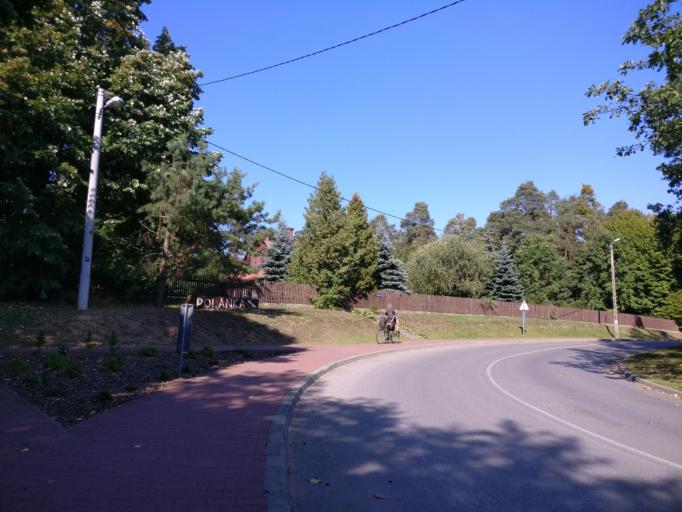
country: PL
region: Masovian Voivodeship
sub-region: Powiat kozienicki
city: Garbatka-Letnisko
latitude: 51.4930
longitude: 21.6244
